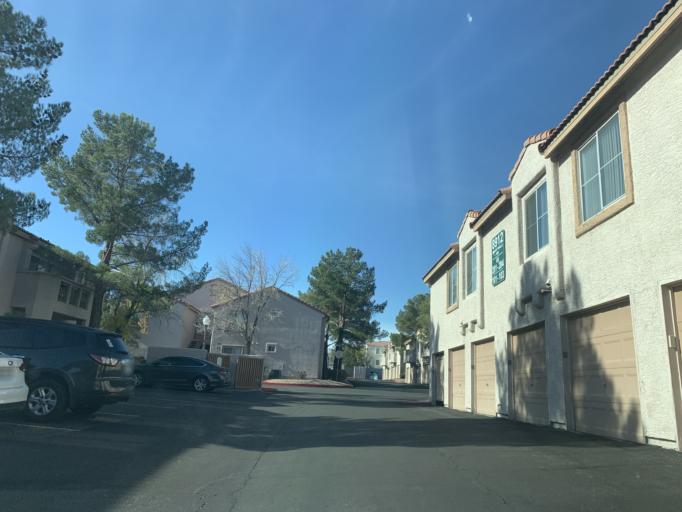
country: US
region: Nevada
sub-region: Clark County
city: Summerlin South
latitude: 36.1308
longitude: -115.2941
